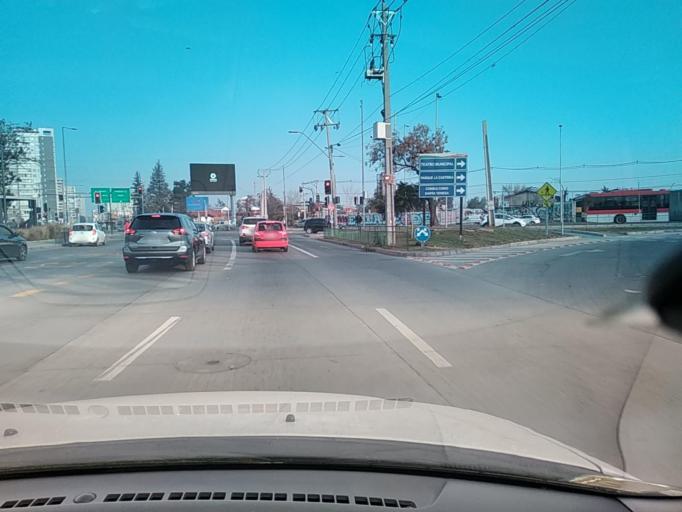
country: CL
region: Santiago Metropolitan
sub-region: Provincia de Santiago
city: Villa Presidente Frei, Nunoa, Santiago, Chile
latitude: -33.5077
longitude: -70.6141
